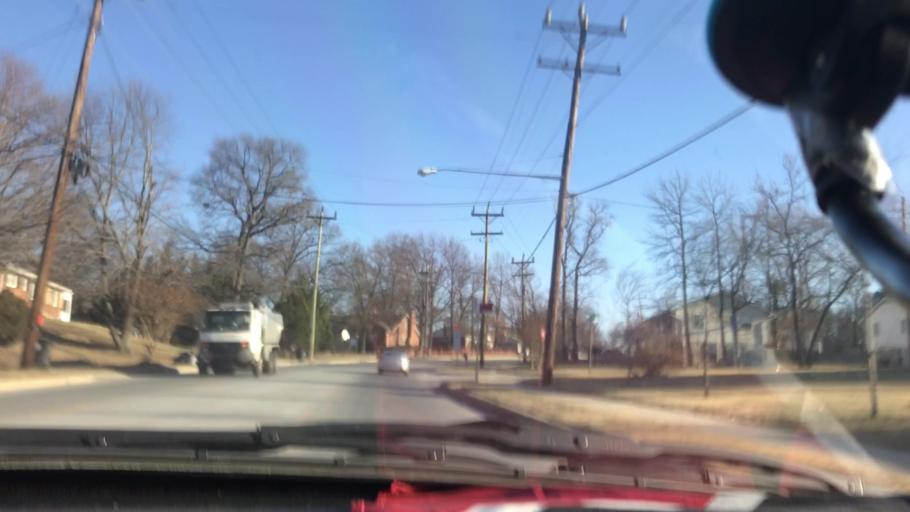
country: US
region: Maryland
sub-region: Prince George's County
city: Morningside
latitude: 38.8317
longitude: -76.8977
